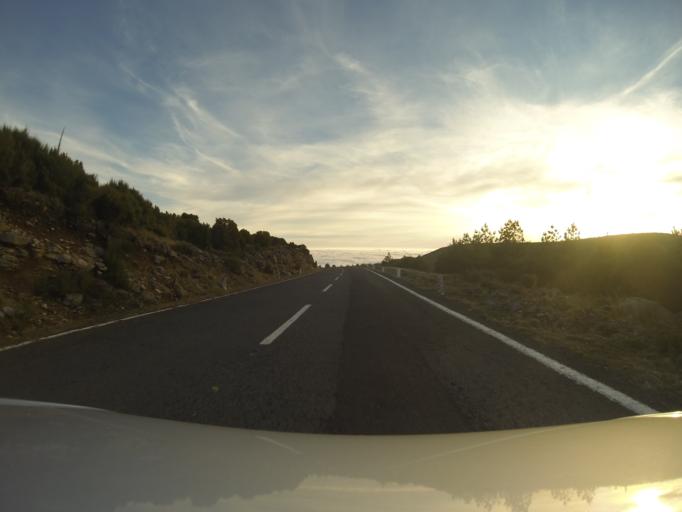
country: PT
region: Madeira
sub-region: Sao Vicente
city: Sao Vicente
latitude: 32.7377
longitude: -17.0607
